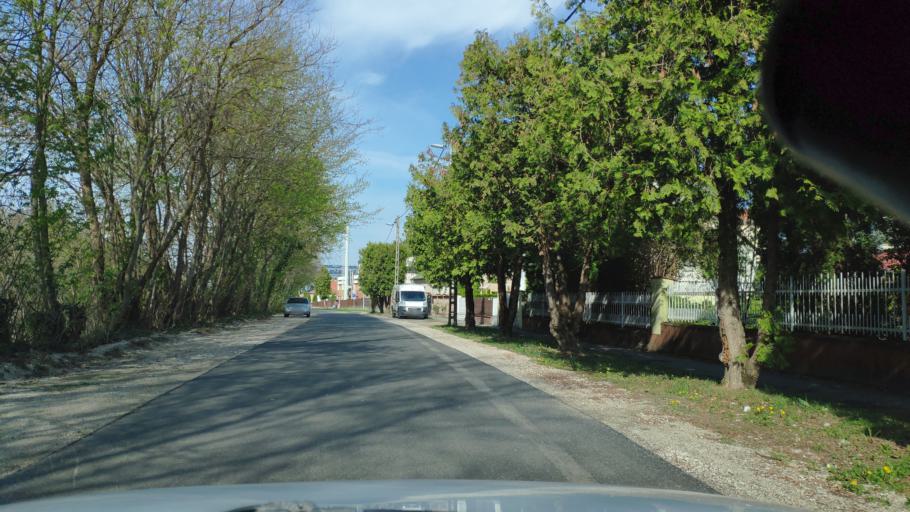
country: HU
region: Zala
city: Nagykanizsa
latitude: 46.4503
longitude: 17.0009
